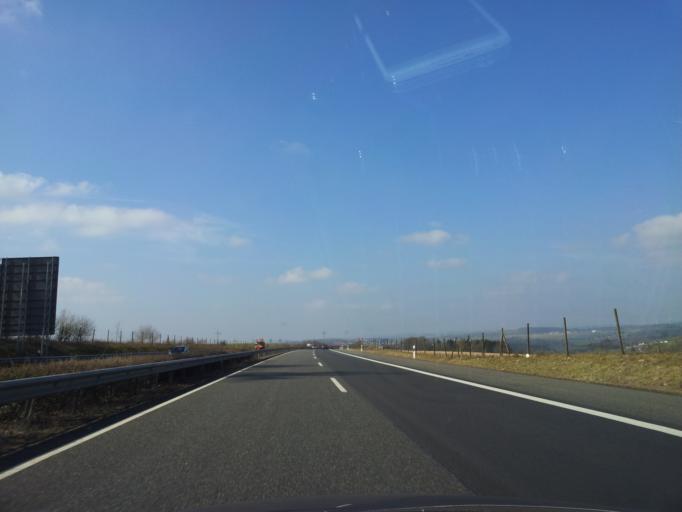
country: DE
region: Rheinland-Pfalz
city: Wilsecker
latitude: 50.0172
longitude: 6.6027
